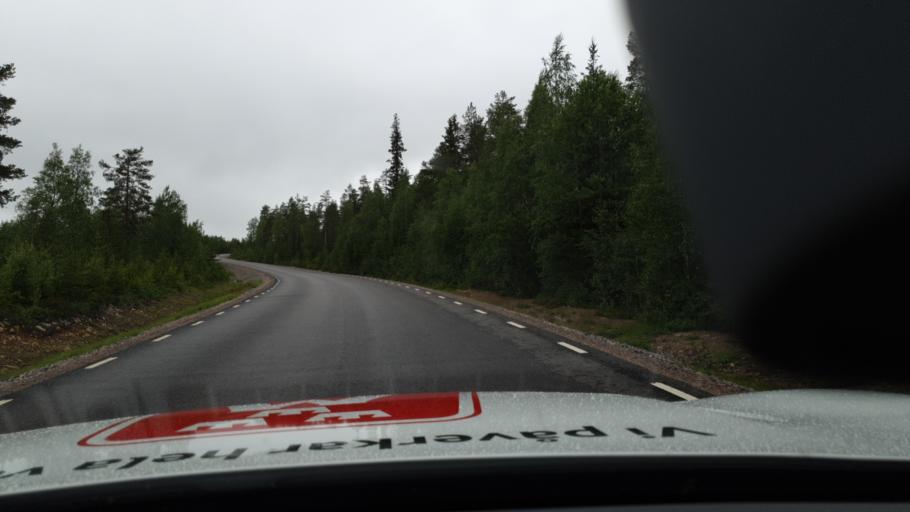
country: SE
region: Norrbotten
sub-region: Overtornea Kommun
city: OEvertornea
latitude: 66.4375
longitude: 23.5076
